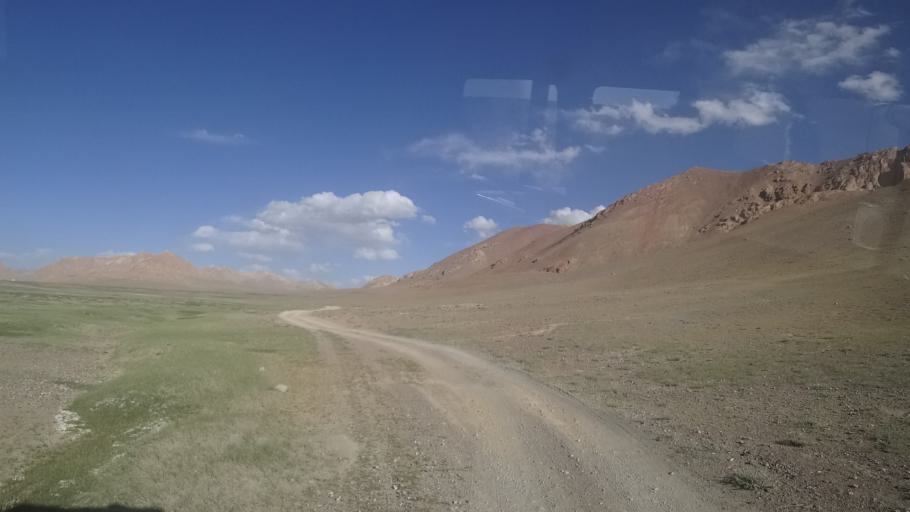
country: TJ
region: Gorno-Badakhshan
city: Murghob
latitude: 37.6568
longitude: 74.1651
